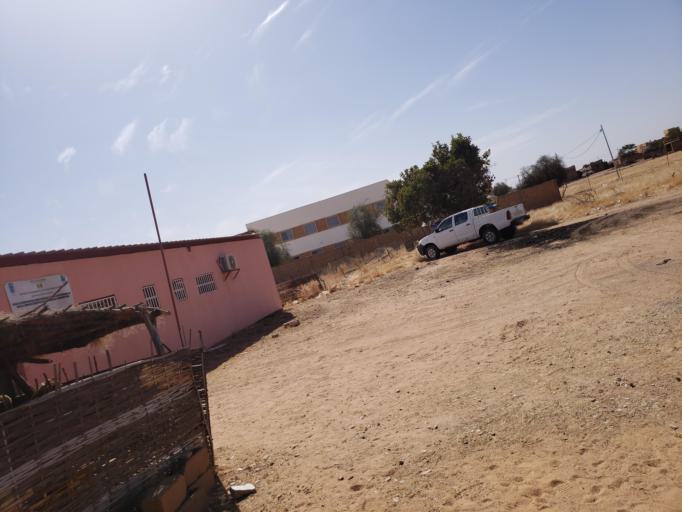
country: SN
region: Matam
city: Ranerou
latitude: 15.2961
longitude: -13.9636
